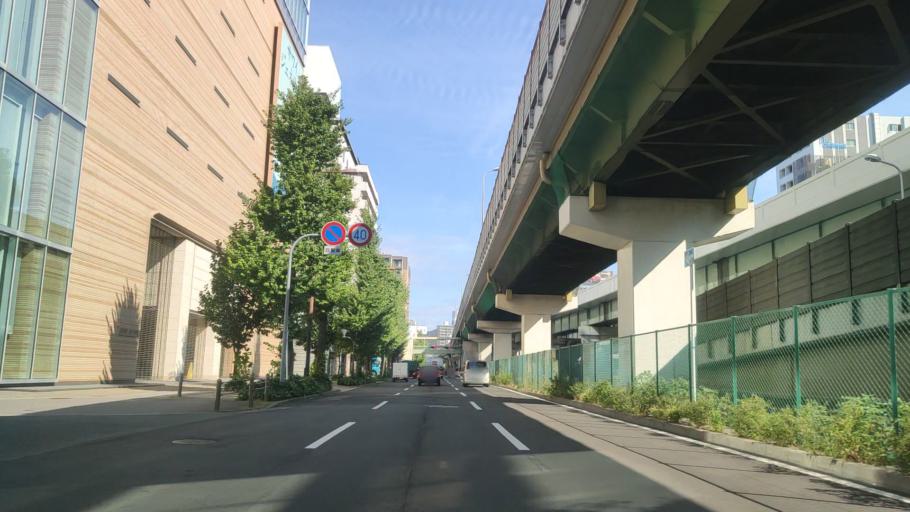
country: JP
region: Osaka
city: Suita
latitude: 34.7387
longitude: 135.4986
